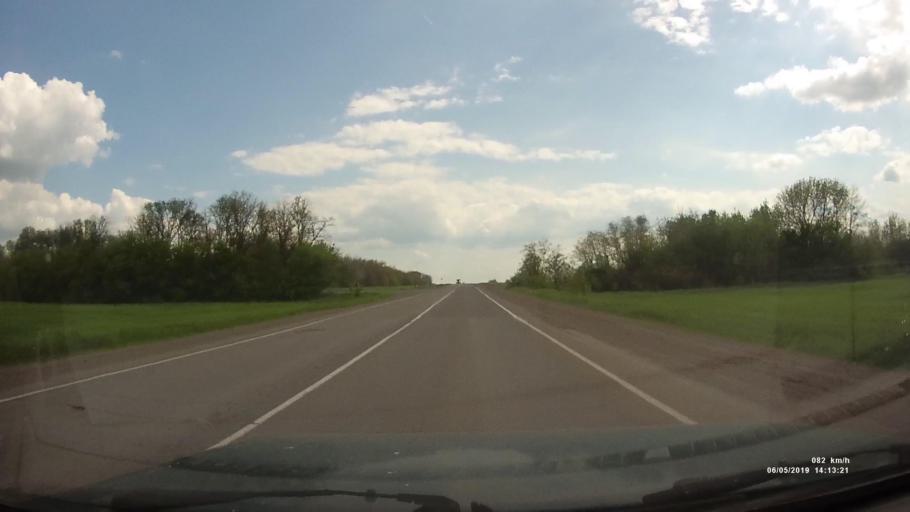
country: RU
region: Rostov
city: Kamenolomni
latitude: 47.6618
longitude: 40.2920
